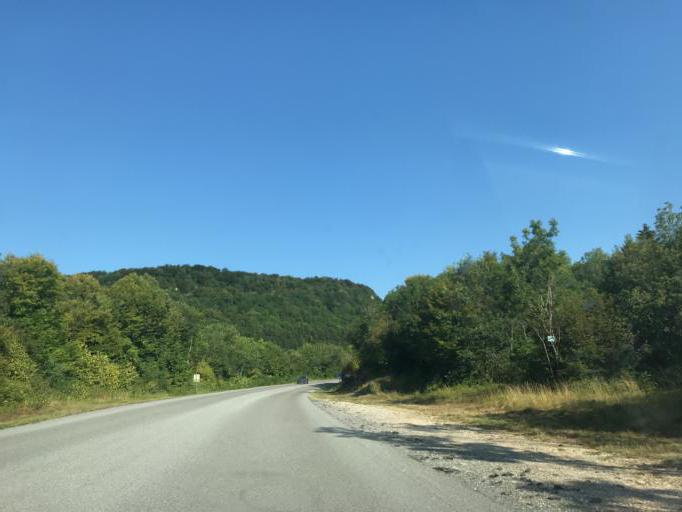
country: FR
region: Franche-Comte
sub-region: Departement du Jura
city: Lavans-les-Saint-Claude
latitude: 46.3840
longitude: 5.7475
